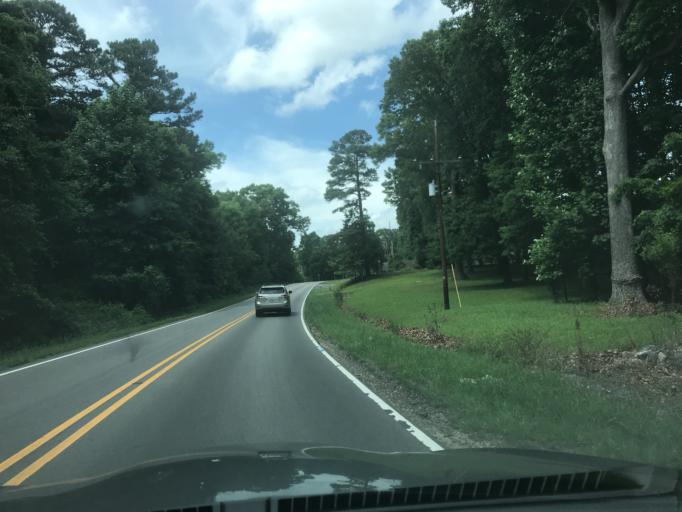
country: US
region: North Carolina
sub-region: Wake County
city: Wake Forest
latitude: 35.9110
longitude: -78.5916
